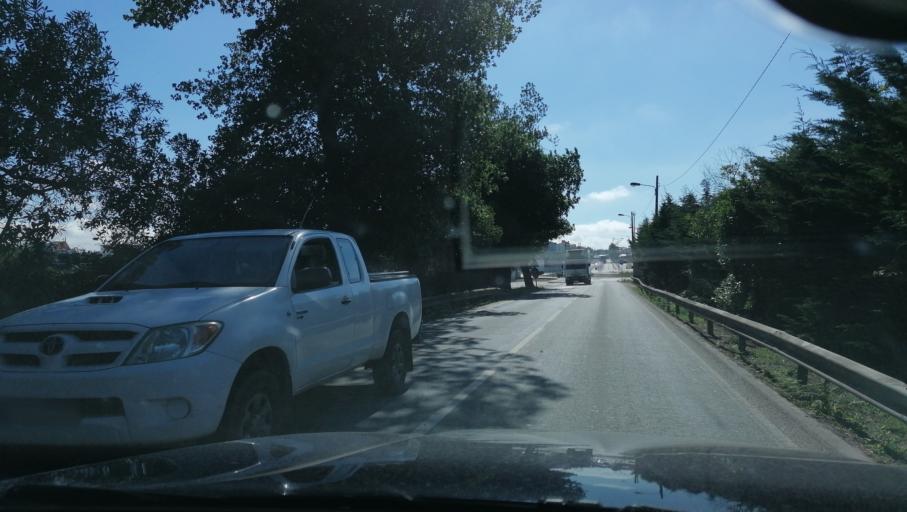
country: PT
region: Aveiro
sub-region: Aveiro
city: Eixo
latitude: 40.6809
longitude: -8.5845
